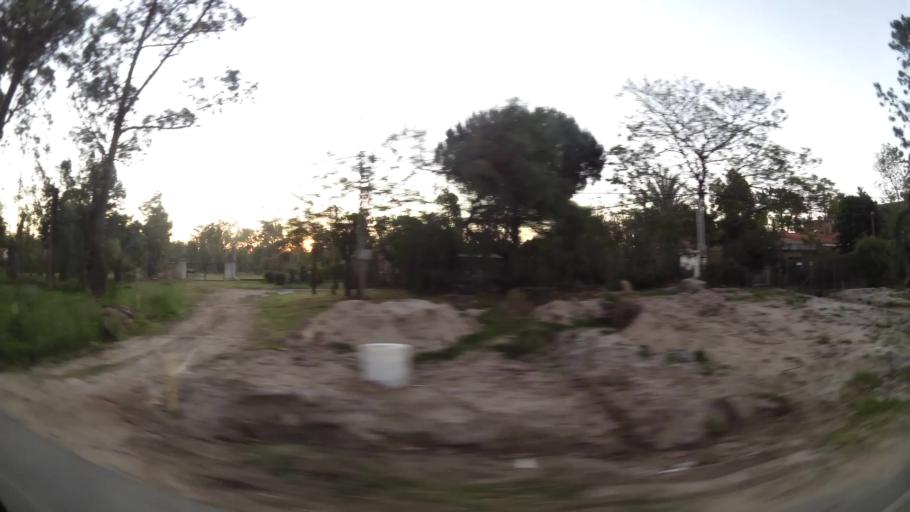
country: UY
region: Canelones
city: Colonia Nicolich
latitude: -34.8262
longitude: -55.9565
